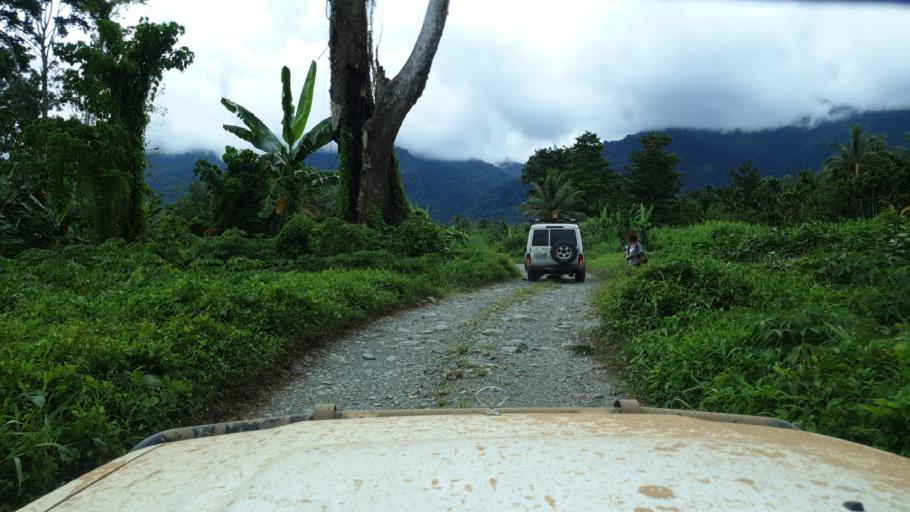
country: PG
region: Northern Province
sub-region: Sohe
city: Kokoda
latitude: -8.9381
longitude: 147.8676
